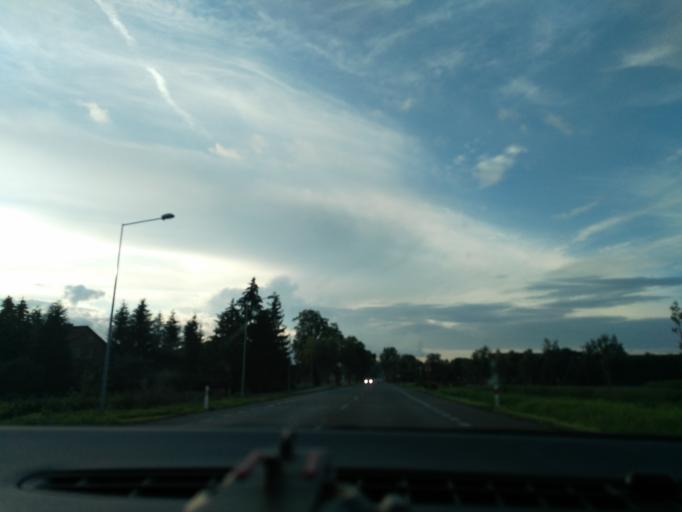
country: PL
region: Lublin Voivodeship
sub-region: Powiat lubelski
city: Niedrzwica Duza
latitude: 51.0850
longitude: 22.3696
